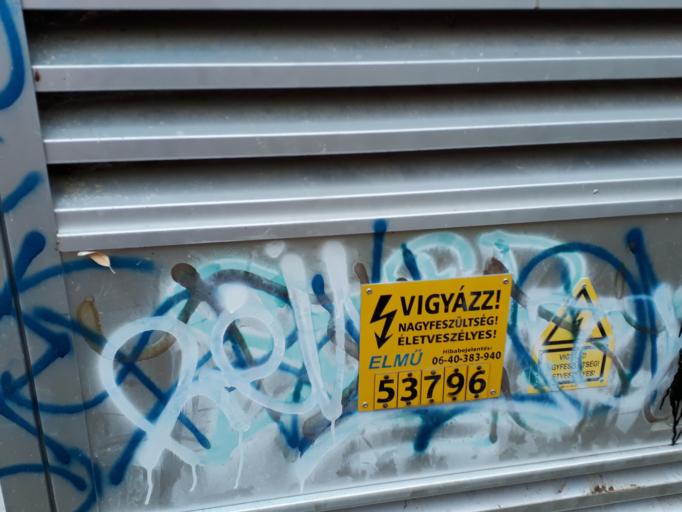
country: HU
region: Budapest
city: Budapest XII. keruelet
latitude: 47.4662
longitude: 18.9963
